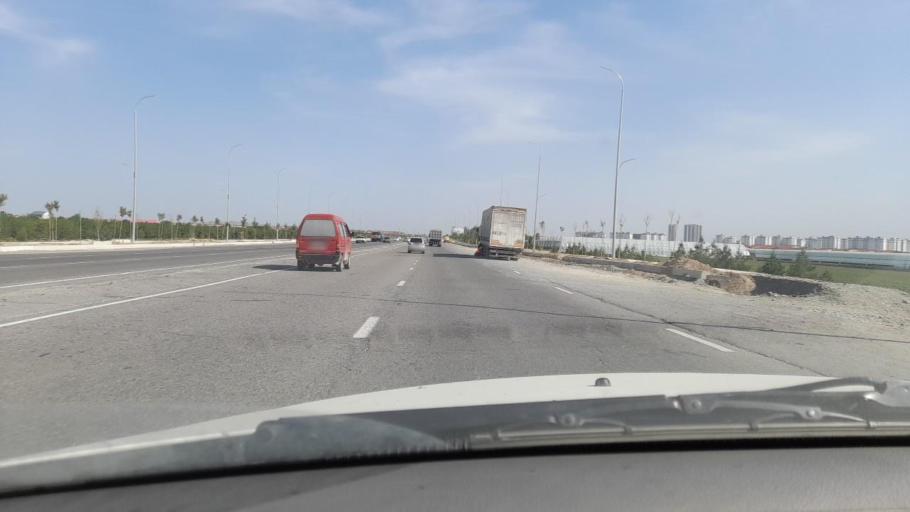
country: UZ
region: Samarqand
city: Daxbet
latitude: 39.7393
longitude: 66.9282
